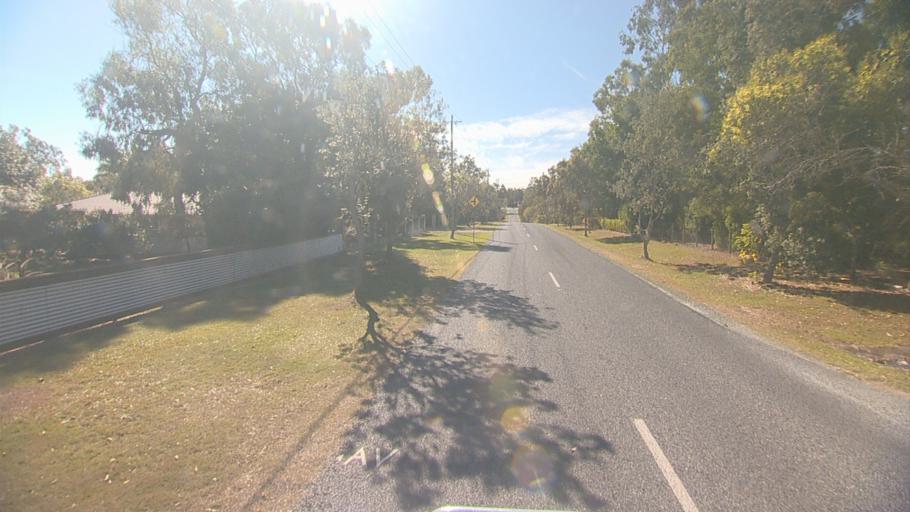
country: AU
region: Queensland
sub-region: Logan
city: North Maclean
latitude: -27.7396
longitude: 152.9594
